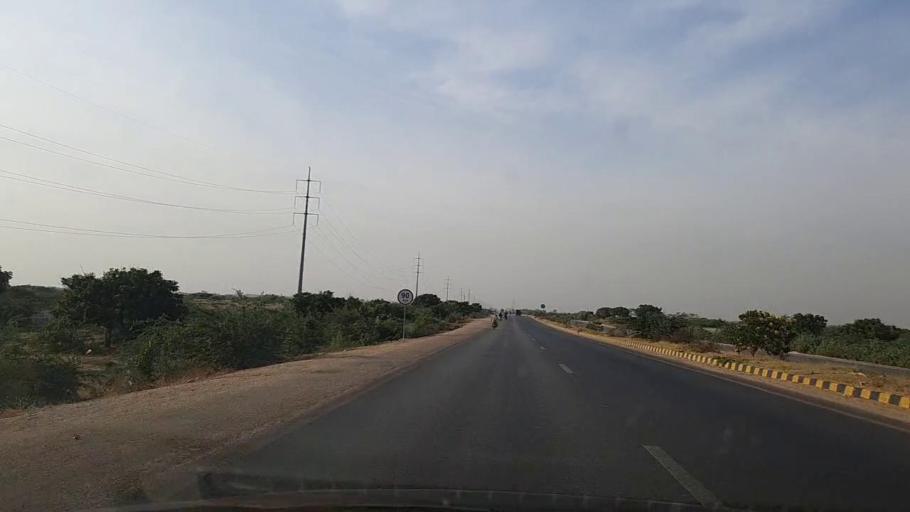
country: PK
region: Sindh
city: Gharo
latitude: 24.7718
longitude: 67.5460
